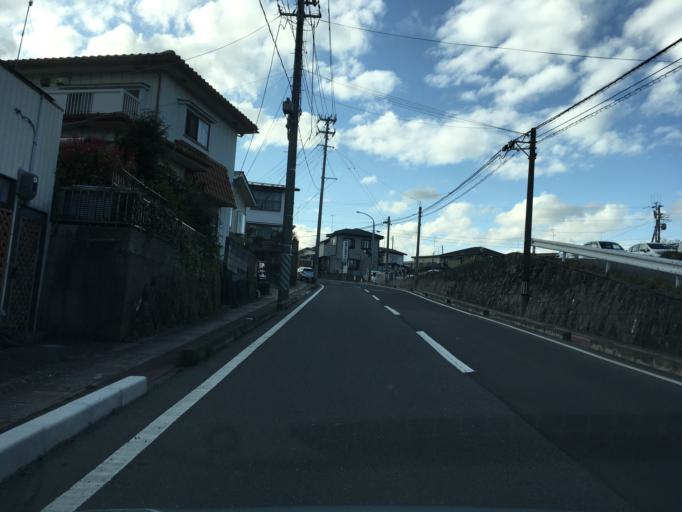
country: JP
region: Miyagi
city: Ishinomaki
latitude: 38.4302
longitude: 141.3018
